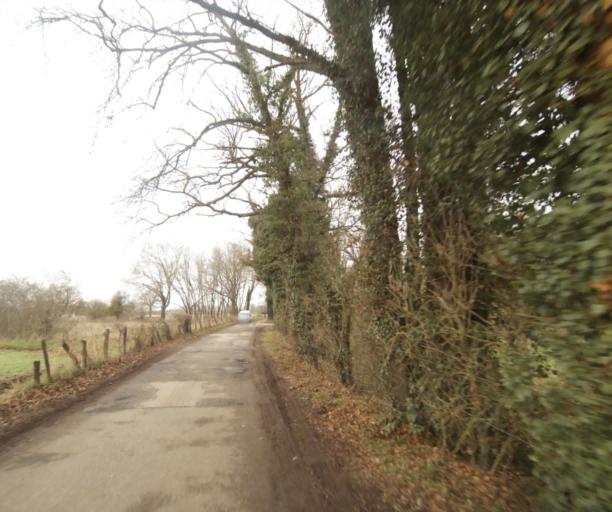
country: FR
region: Rhone-Alpes
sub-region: Departement de la Loire
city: Perreux
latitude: 46.0621
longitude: 4.1051
